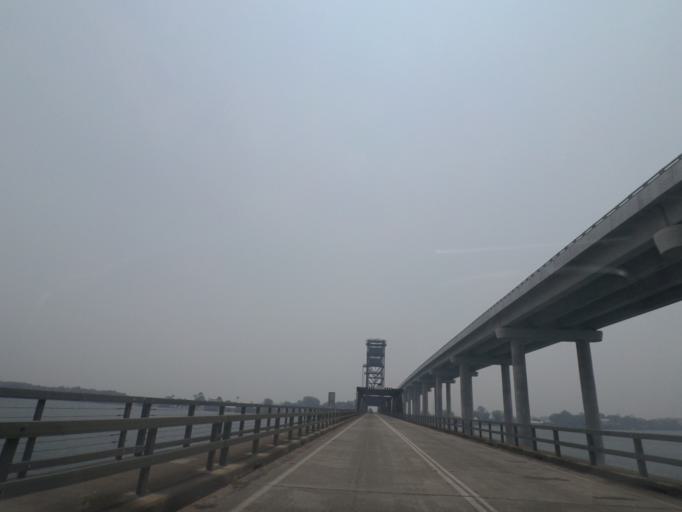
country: AU
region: New South Wales
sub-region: Clarence Valley
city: Maclean
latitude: -29.4319
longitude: 153.2408
